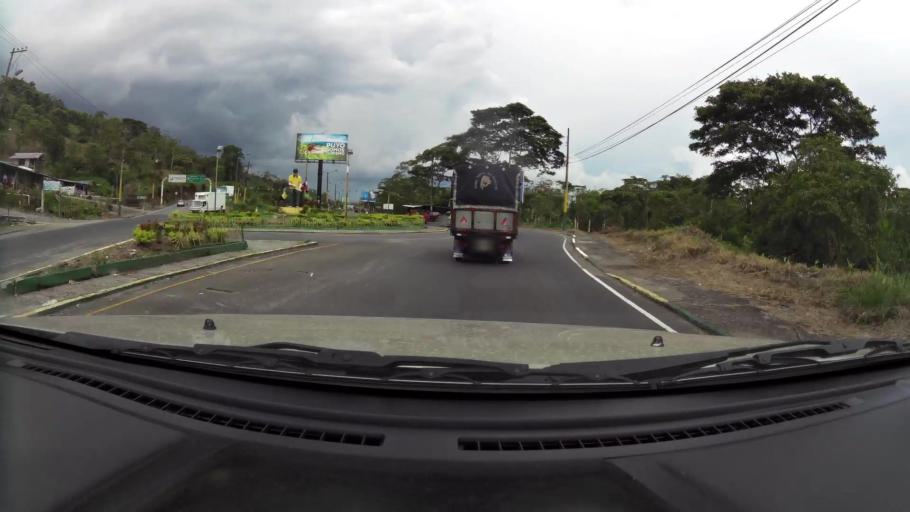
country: EC
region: Pastaza
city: Puyo
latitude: -1.5022
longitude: -78.0231
